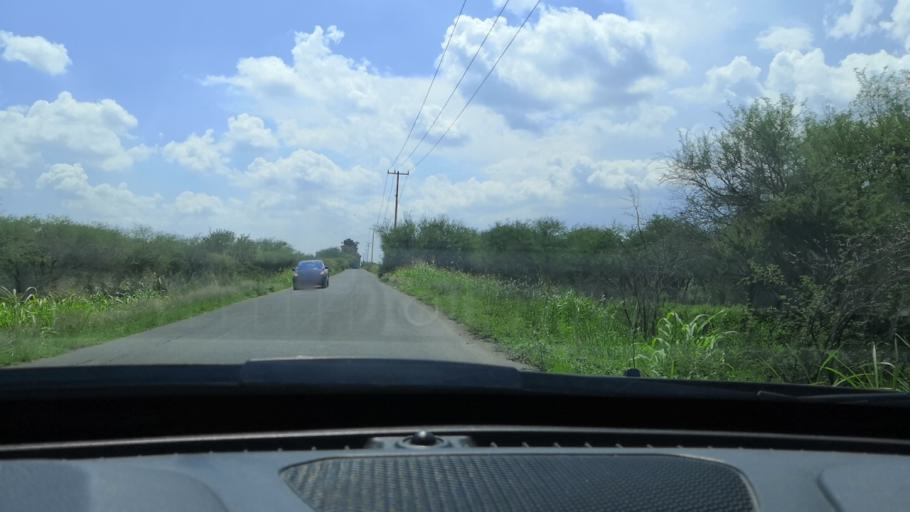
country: MX
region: Guanajuato
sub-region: Leon
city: El CERESO
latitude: 20.9914
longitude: -101.6544
